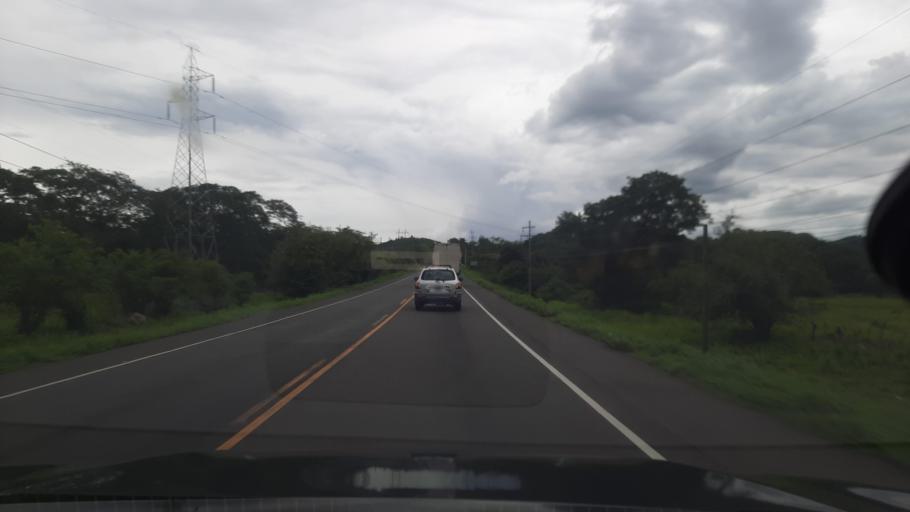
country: HN
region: Choluteca
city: Marcovia
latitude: 13.3702
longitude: -87.2935
